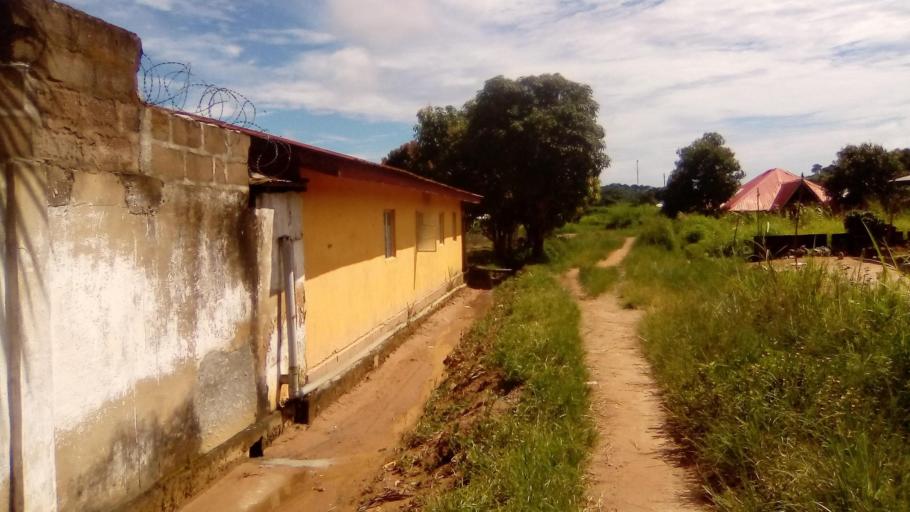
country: SL
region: Eastern Province
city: Koidu
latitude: 8.6370
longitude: -10.9925
